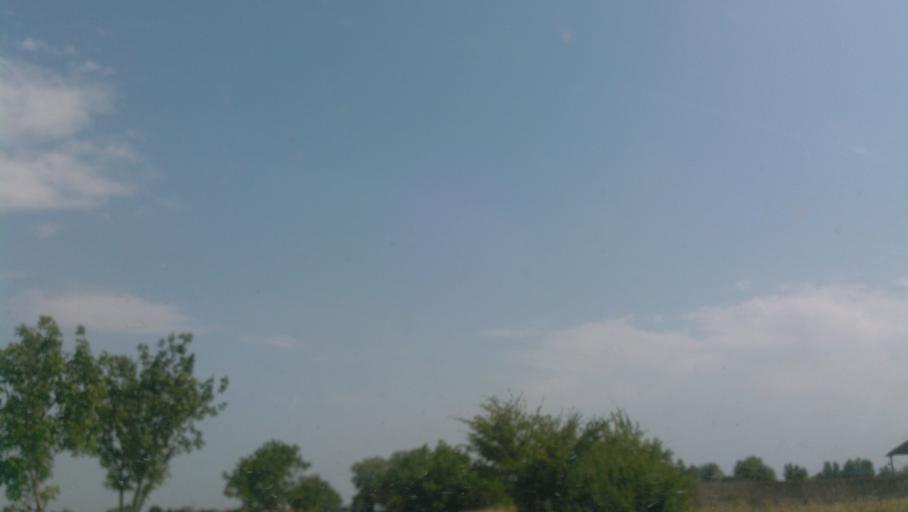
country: SK
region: Trnavsky
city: Dunajska Streda
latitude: 48.0446
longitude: 17.4954
